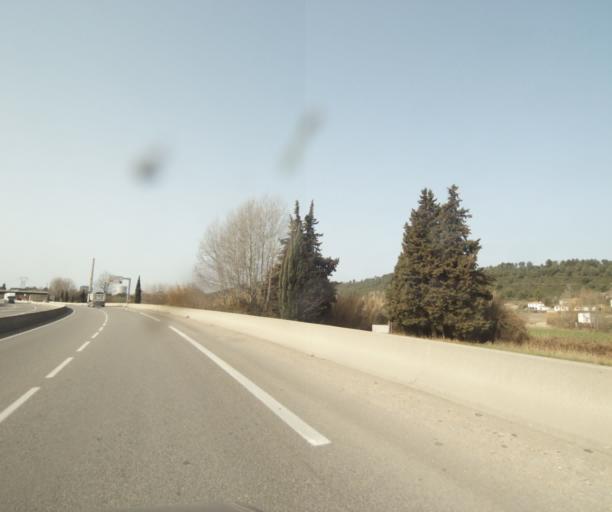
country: FR
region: Provence-Alpes-Cote d'Azur
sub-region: Departement des Bouches-du-Rhone
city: Meyreuil
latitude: 43.4758
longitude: 5.5216
